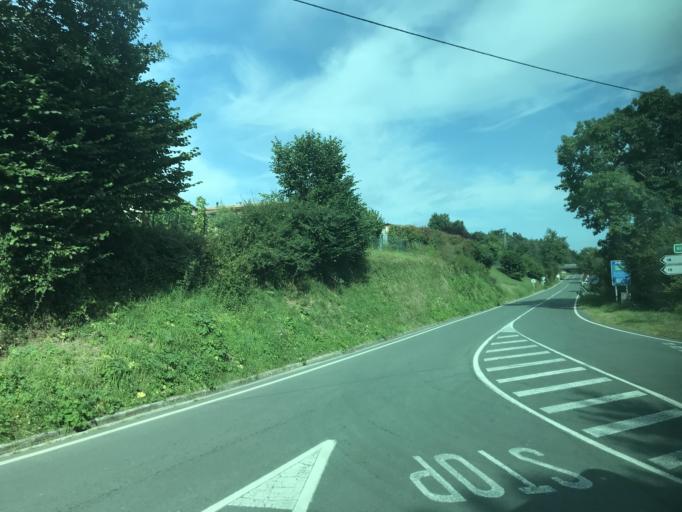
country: ES
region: Basque Country
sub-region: Bizkaia
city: Otxandio
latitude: 43.0446
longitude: -2.6541
